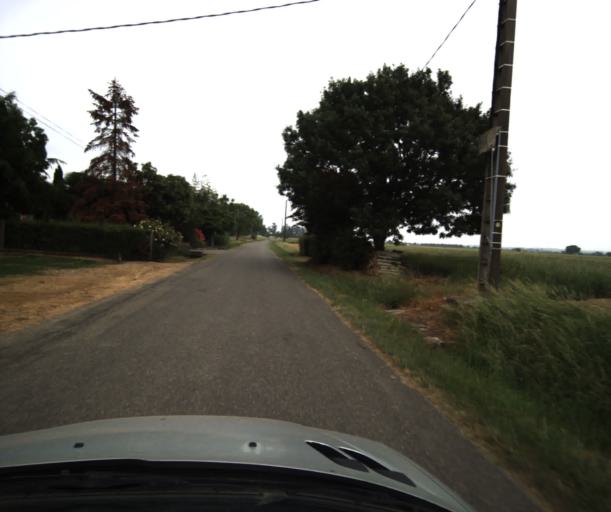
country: FR
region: Midi-Pyrenees
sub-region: Departement du Tarn-et-Garonne
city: Saint-Nicolas-de-la-Grave
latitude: 44.0480
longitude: 1.0244
